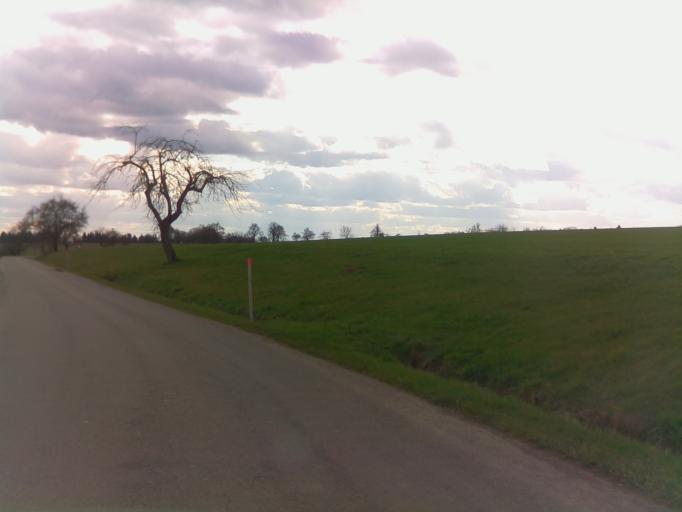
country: DE
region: Baden-Wuerttemberg
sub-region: Regierungsbezirk Stuttgart
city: Alfdorf
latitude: 48.8392
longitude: 9.6769
